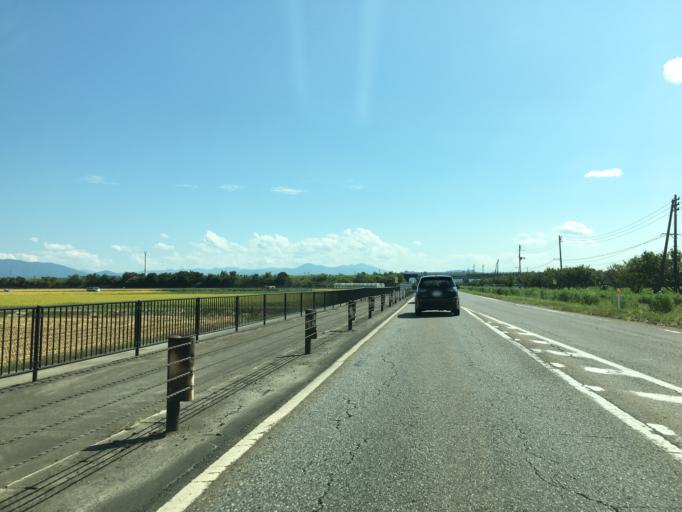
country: JP
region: Niigata
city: Niitsu-honcho
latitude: 37.8243
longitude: 139.0984
